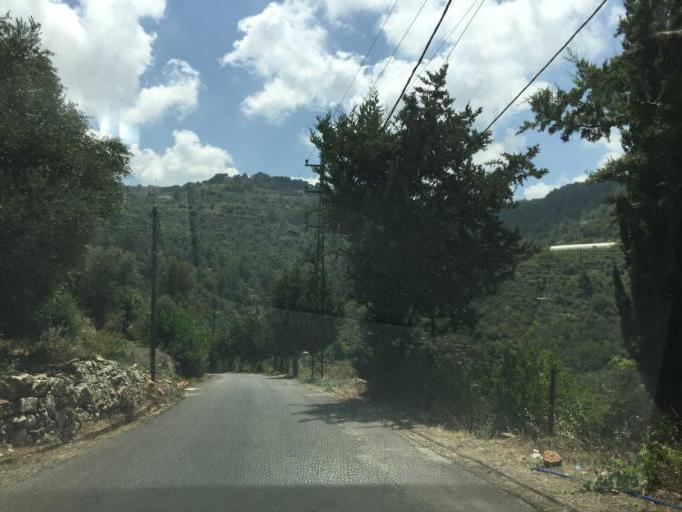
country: LB
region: Mont-Liban
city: Beit ed Dine
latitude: 33.6955
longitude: 35.5702
